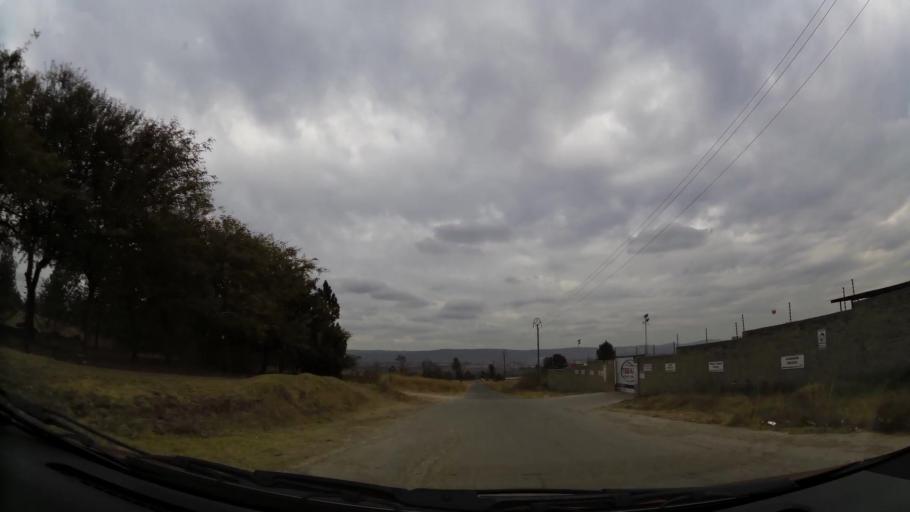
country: ZA
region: Gauteng
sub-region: West Rand District Municipality
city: Muldersdriseloop
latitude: -26.0537
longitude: 27.8905
